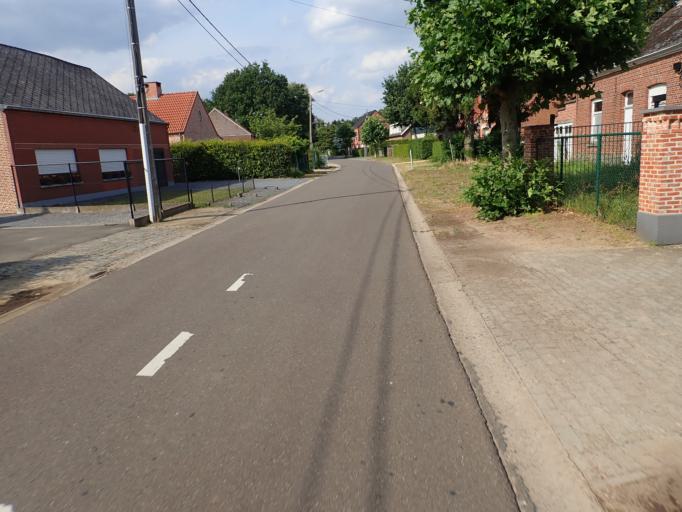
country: BE
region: Flanders
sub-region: Provincie Vlaams-Brabant
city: Keerbergen
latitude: 51.0119
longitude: 4.6310
